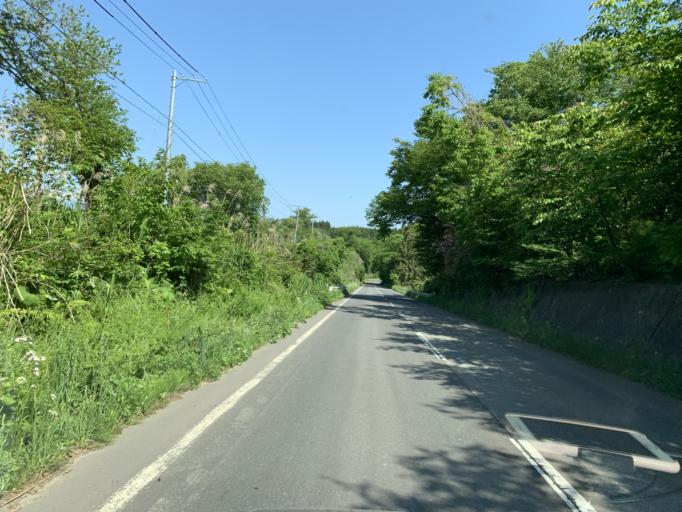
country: JP
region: Iwate
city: Mizusawa
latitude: 39.0615
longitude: 141.0618
